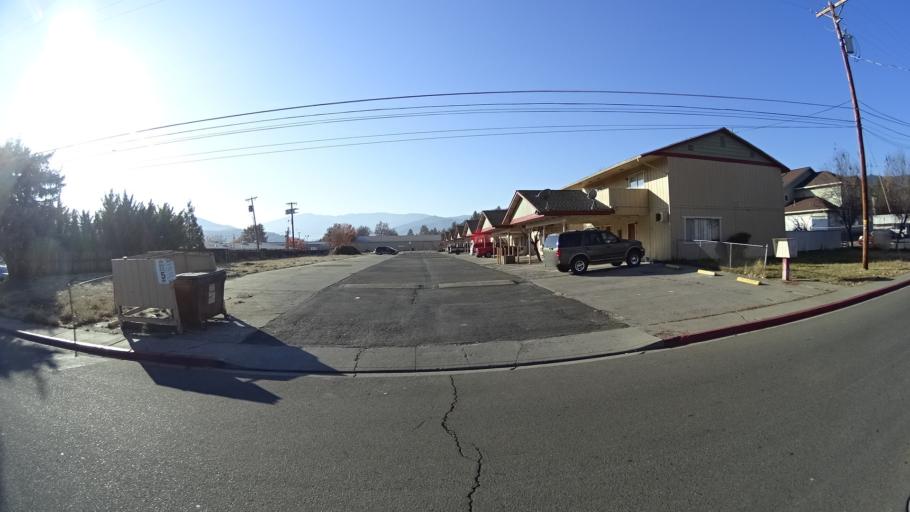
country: US
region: California
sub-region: Siskiyou County
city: Yreka
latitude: 41.7186
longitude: -122.6433
